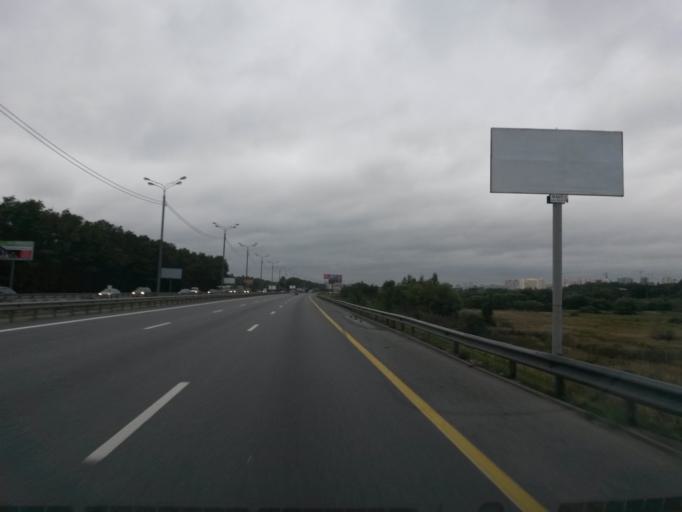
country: RU
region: Moskovskaya
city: Vidnoye
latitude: 55.5218
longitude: 37.7055
